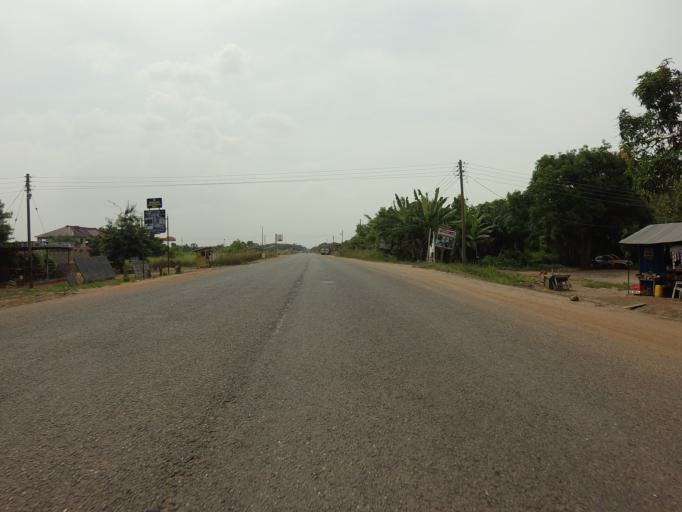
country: GH
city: Akropong
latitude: 5.9084
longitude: -0.0664
